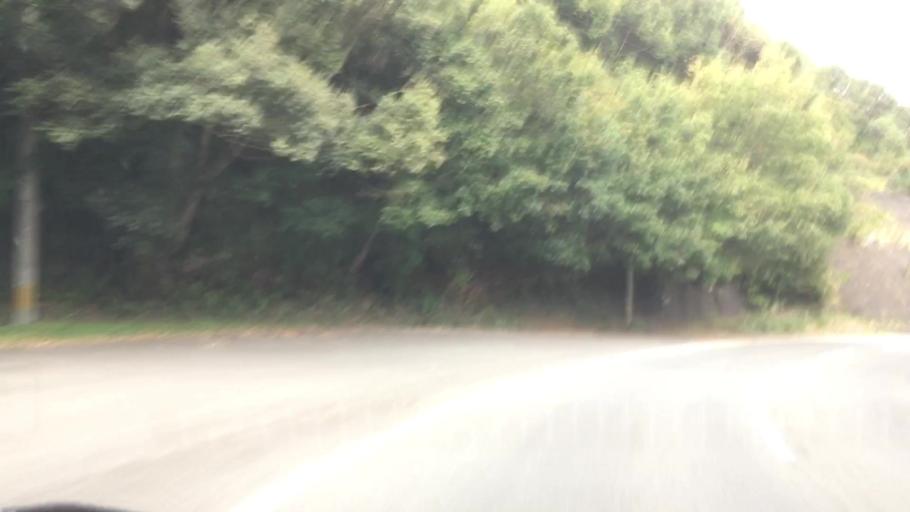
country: JP
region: Nagasaki
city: Sasebo
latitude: 32.9795
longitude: 129.7121
